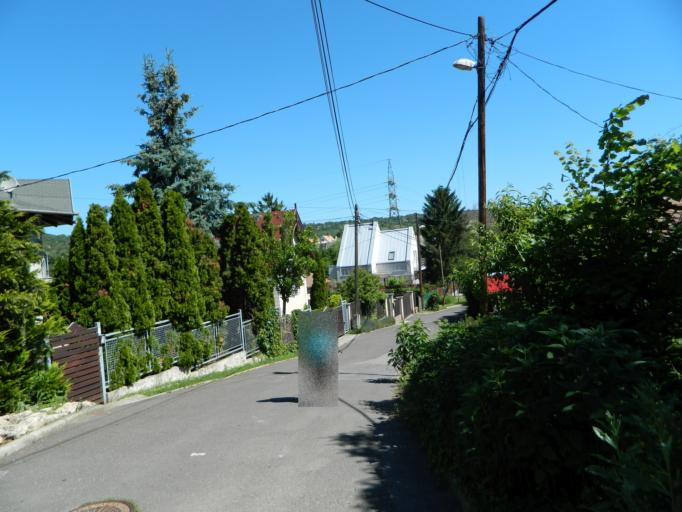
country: HU
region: Pest
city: Budakalasz
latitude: 47.5940
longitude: 19.0418
